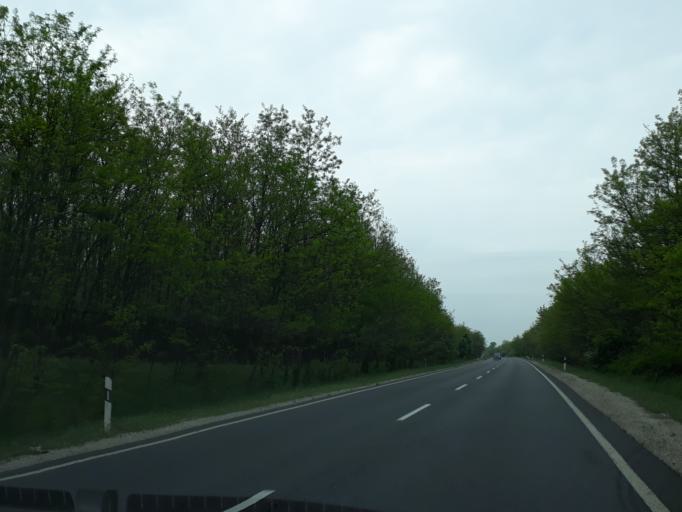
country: HU
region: Szabolcs-Szatmar-Bereg
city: Nyirtass
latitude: 48.1031
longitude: 21.9877
